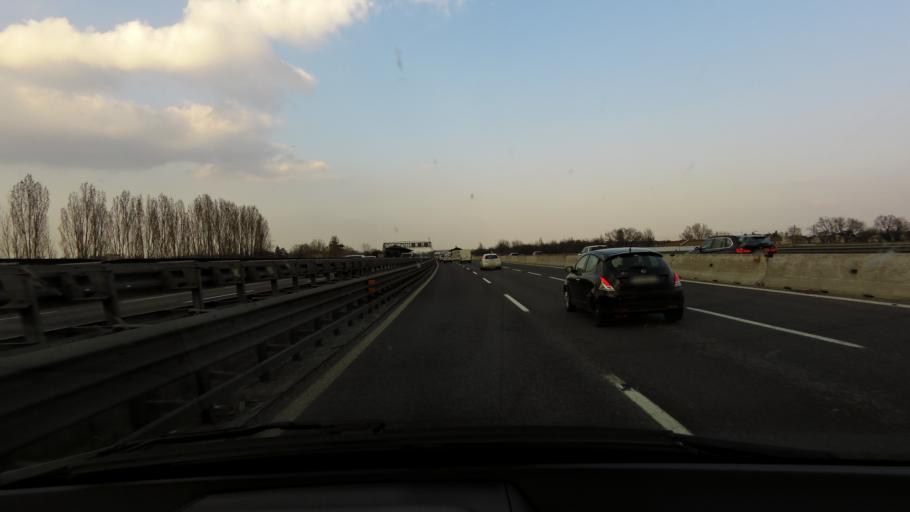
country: IT
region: Emilia-Romagna
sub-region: Provincia di Bologna
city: Trebbo
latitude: 44.5255
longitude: 11.3101
